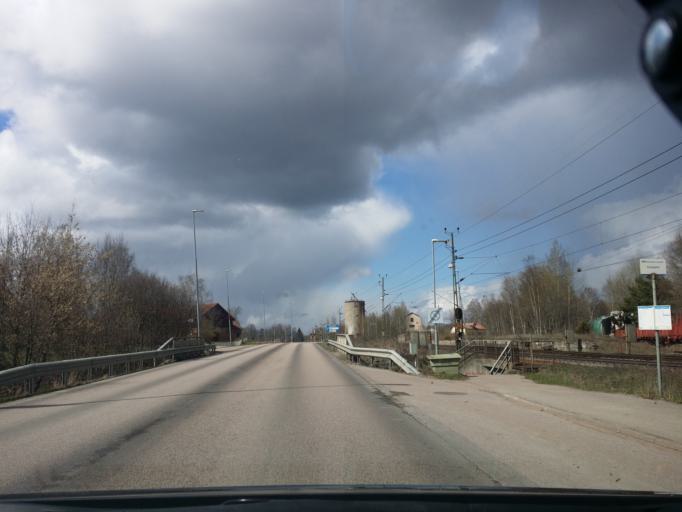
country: SE
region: Vaestmanland
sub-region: Sala Kommun
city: Sala
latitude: 59.9277
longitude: 16.5976
